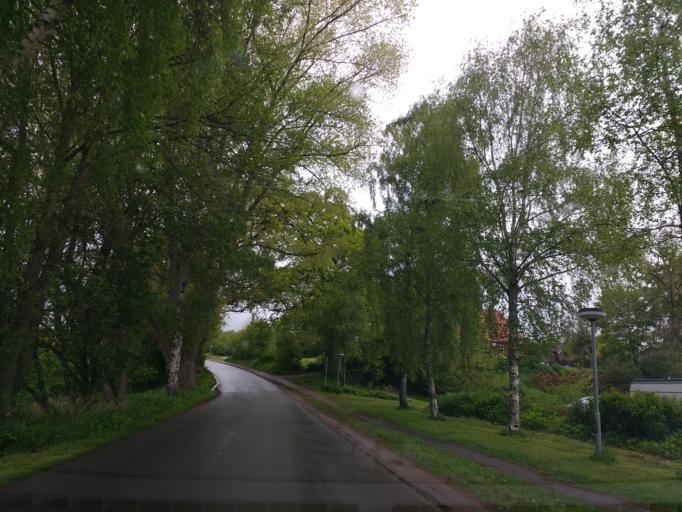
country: DE
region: Schleswig-Holstein
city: Loose
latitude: 54.4972
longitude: 9.9357
